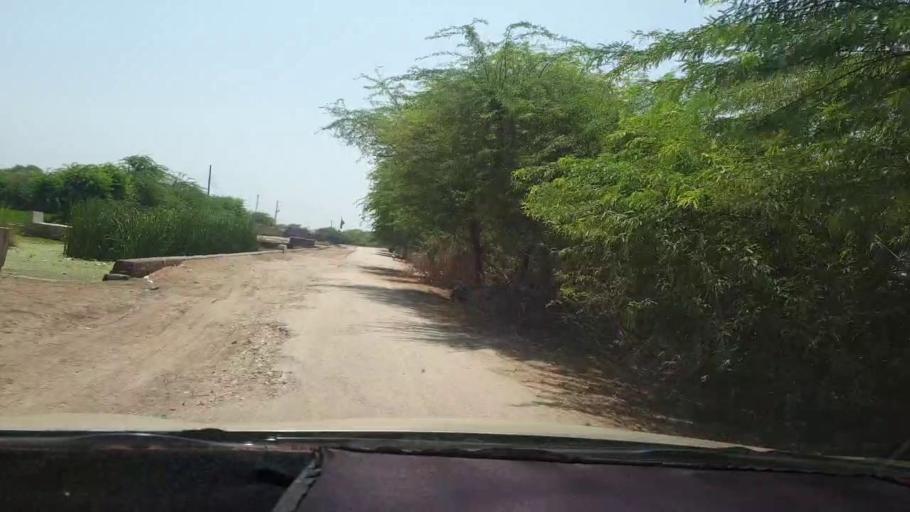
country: PK
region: Sindh
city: Shahdadkot
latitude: 27.8361
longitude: 67.9390
